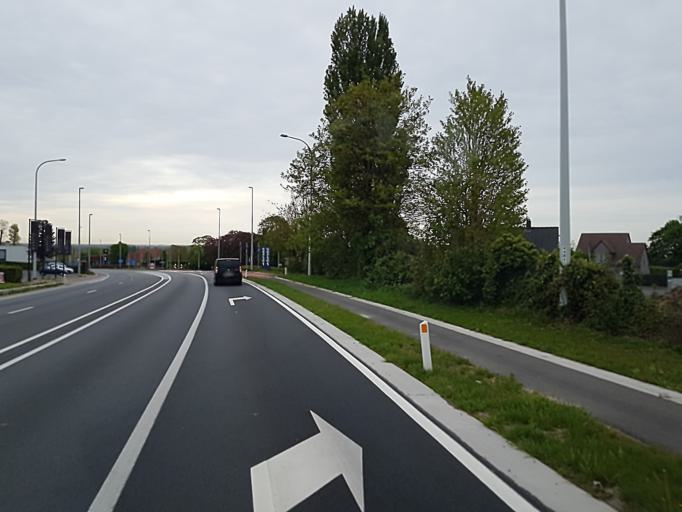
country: BE
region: Flanders
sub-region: Provincie West-Vlaanderen
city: Tielt
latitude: 50.9985
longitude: 3.3449
